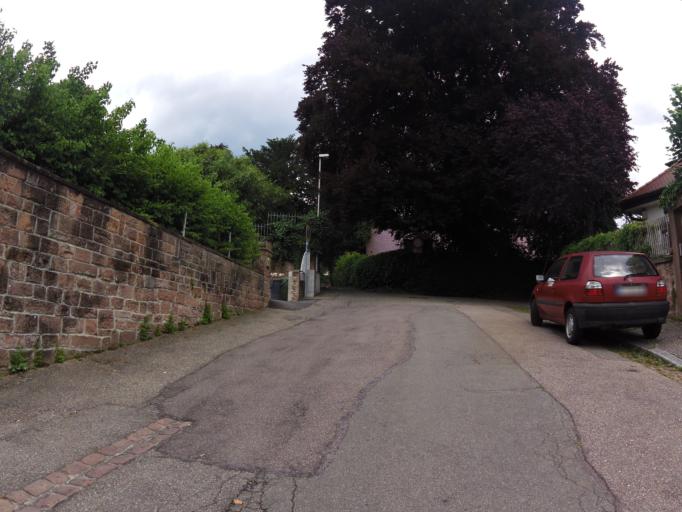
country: DE
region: Baden-Wuerttemberg
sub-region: Freiburg Region
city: Lahr
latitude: 48.3430
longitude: 7.8748
